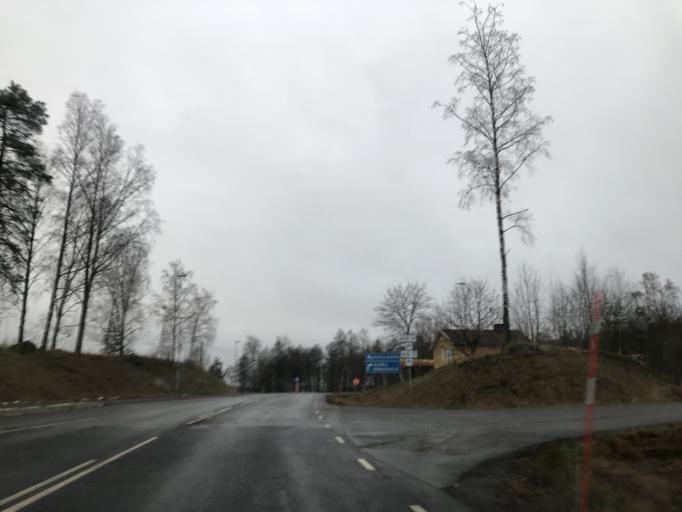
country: SE
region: Vaestra Goetaland
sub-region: Ulricehamns Kommun
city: Ulricehamn
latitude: 57.8145
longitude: 13.2894
